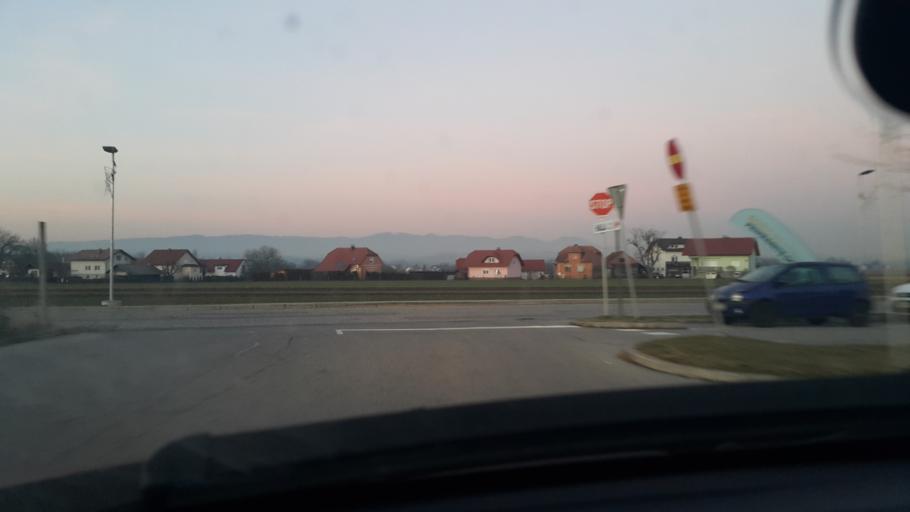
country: SI
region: Brezice
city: Brezice
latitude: 45.9184
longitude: 15.5955
